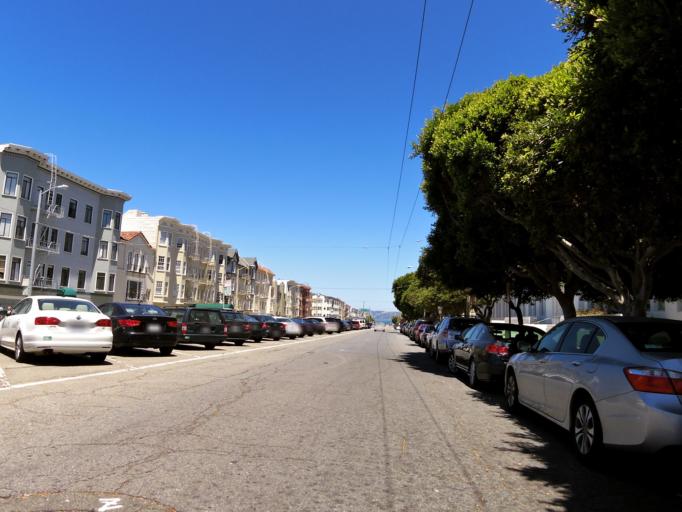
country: US
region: California
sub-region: San Francisco County
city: San Francisco
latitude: 37.8013
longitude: -122.4363
